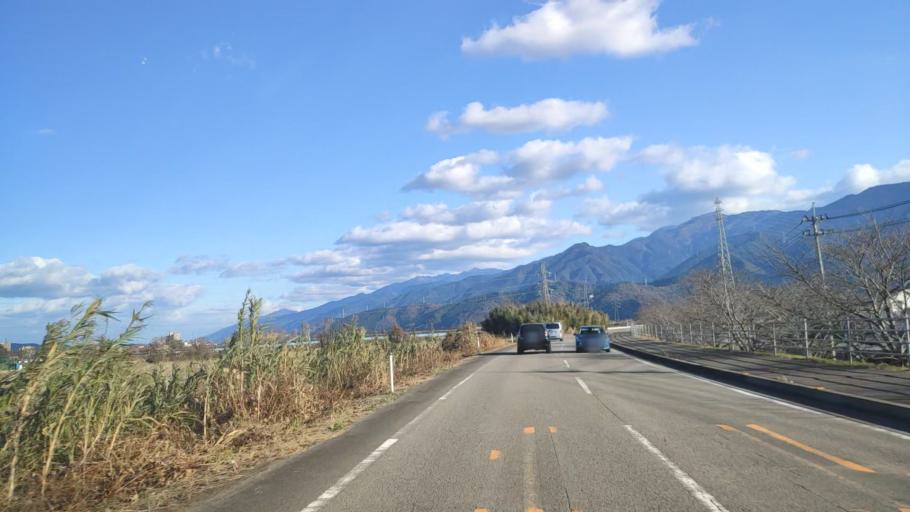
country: JP
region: Ehime
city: Saijo
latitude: 33.9105
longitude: 133.1662
